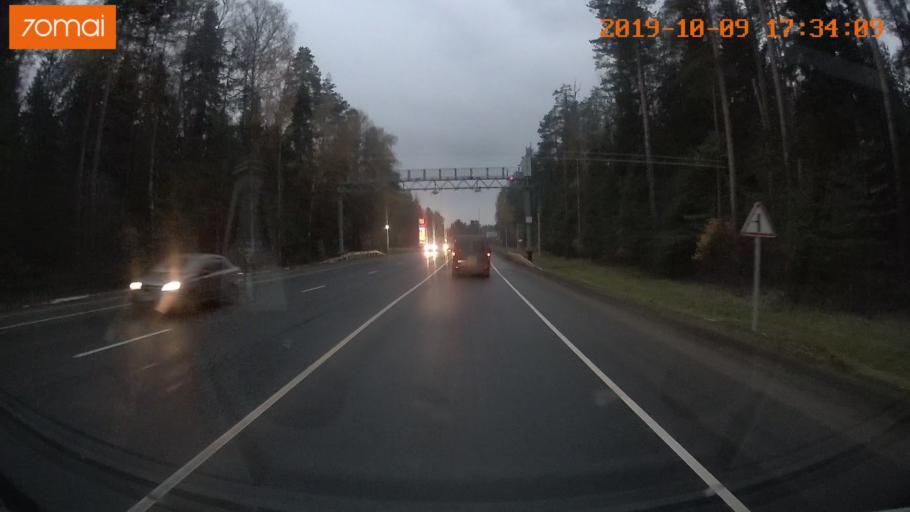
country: RU
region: Ivanovo
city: Bogorodskoye
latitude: 57.1092
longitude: 41.0147
